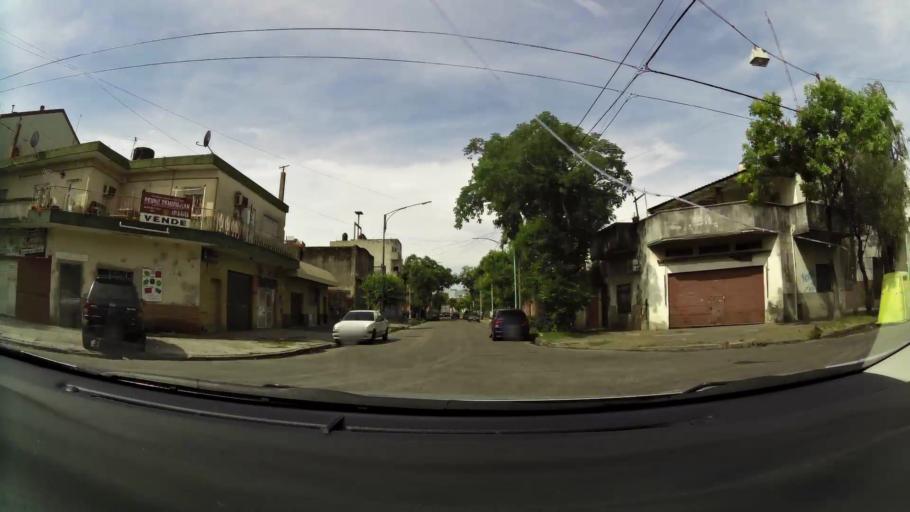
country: AR
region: Buenos Aires F.D.
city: Villa Lugano
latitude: -34.6541
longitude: -58.4331
